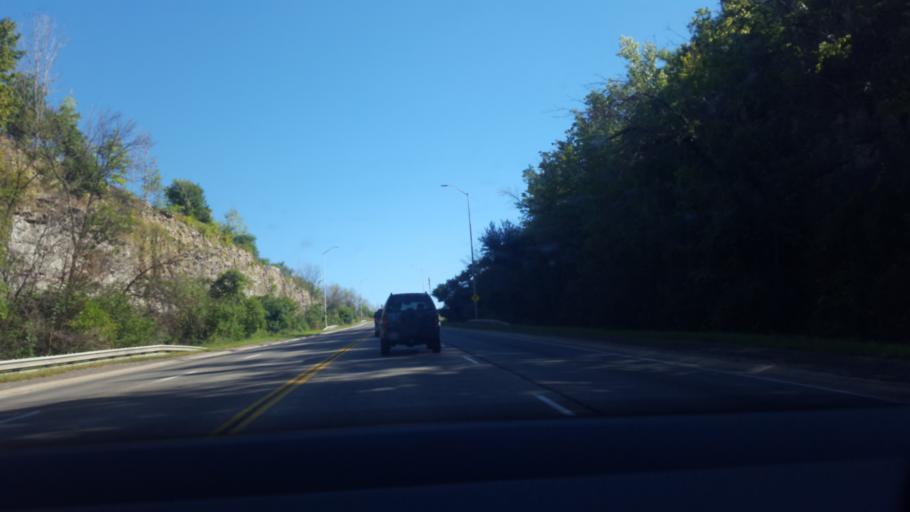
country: CA
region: Ontario
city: Hamilton
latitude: 43.2076
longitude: -79.7660
